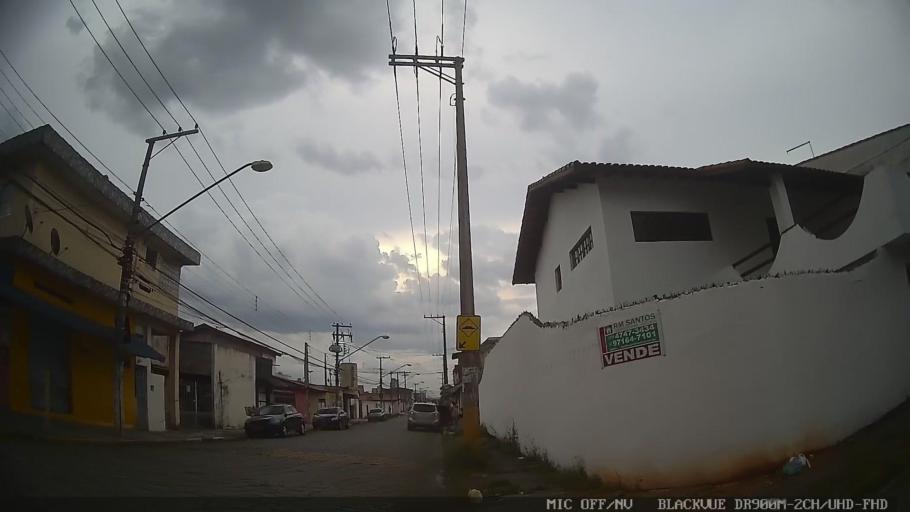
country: BR
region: Sao Paulo
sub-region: Suzano
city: Suzano
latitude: -23.5423
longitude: -46.2968
